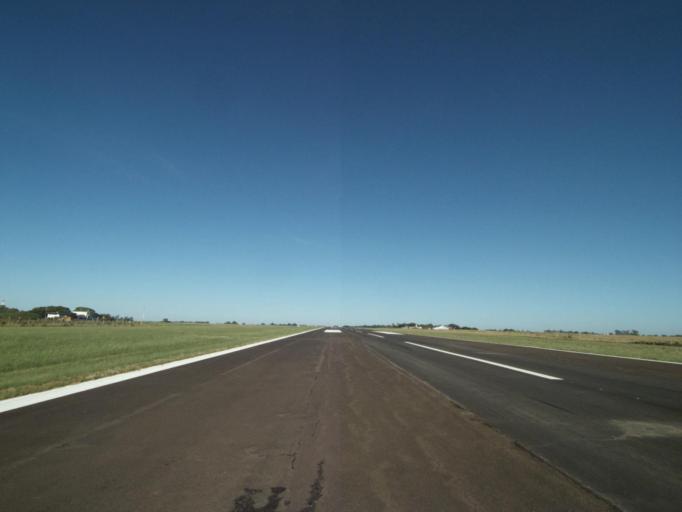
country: BR
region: Rio Grande do Sul
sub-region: Uruguaiana
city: Uruguaiana
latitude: -29.7817
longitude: -57.0321
